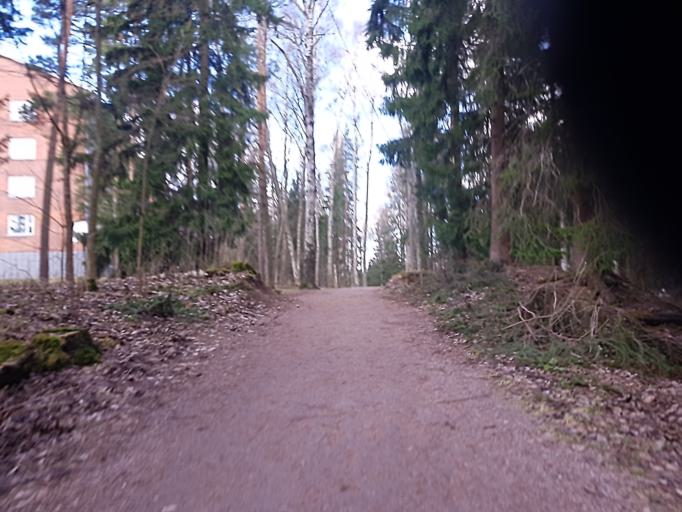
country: FI
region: Uusimaa
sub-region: Helsinki
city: Teekkarikylae
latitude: 60.2327
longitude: 24.8949
